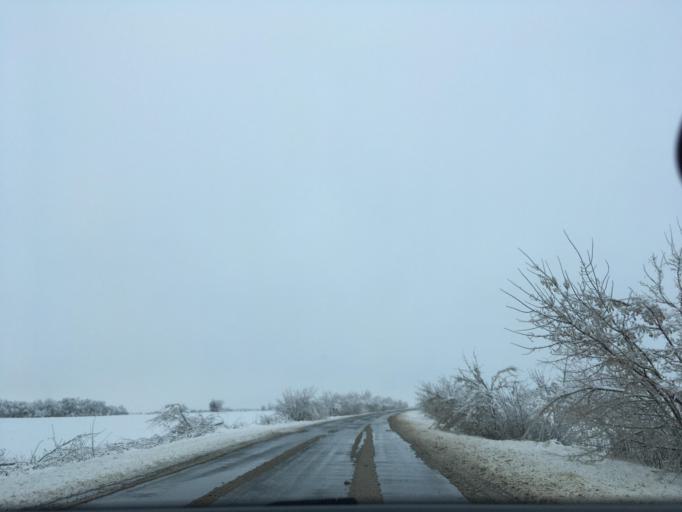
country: RU
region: Voronezj
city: Ol'khovatka
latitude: 50.1235
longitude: 39.1755
